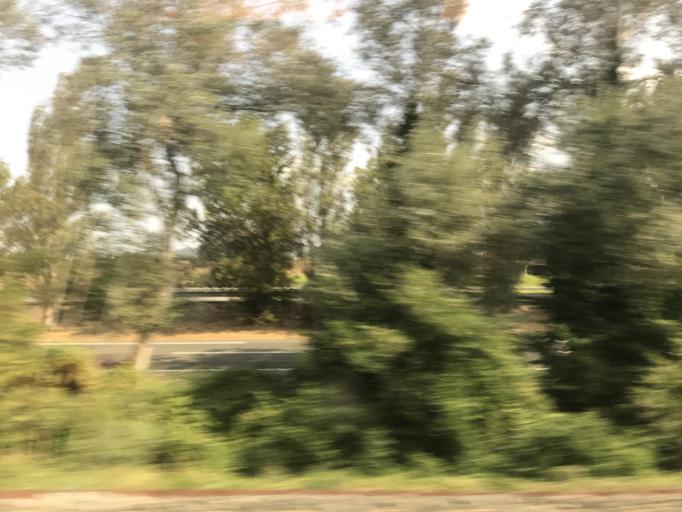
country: ES
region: Basque Country
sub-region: Provincia de Alava
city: Arminon
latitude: 42.7536
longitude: -2.8383
